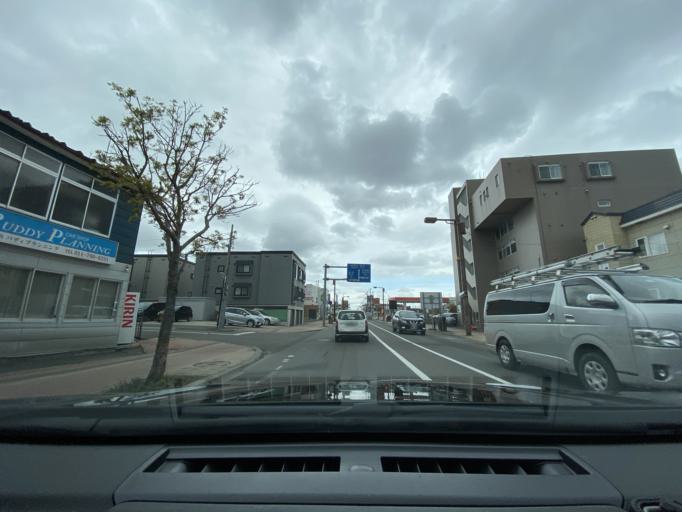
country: JP
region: Hokkaido
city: Sapporo
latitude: 43.0910
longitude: 141.3189
